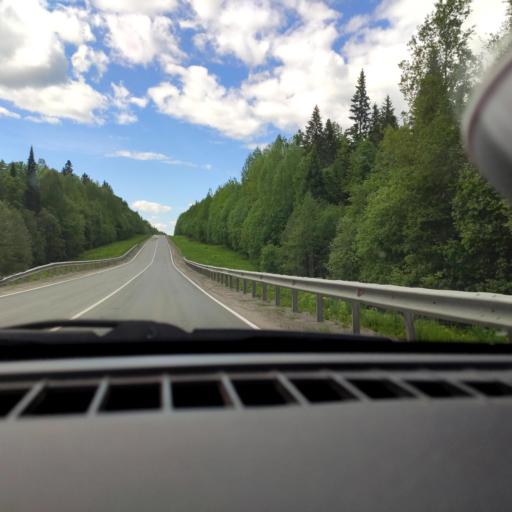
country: RU
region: Perm
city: Perm
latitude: 58.1651
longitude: 56.2409
